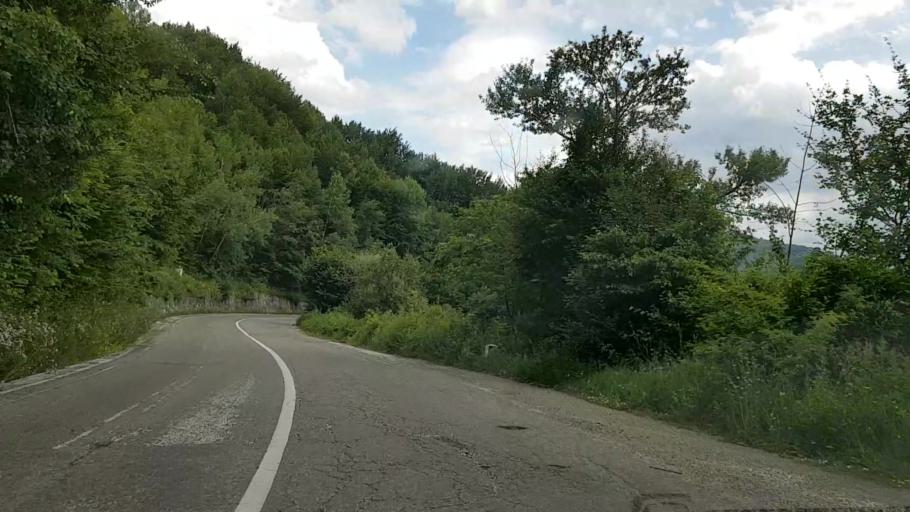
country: RO
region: Neamt
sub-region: Comuna Pangarati
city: Pangarati
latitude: 46.9606
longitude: 26.1222
